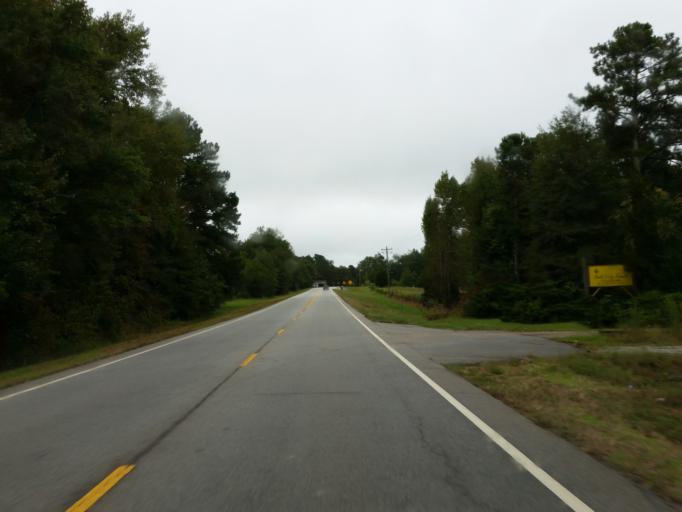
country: US
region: Georgia
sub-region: Lamar County
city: Barnesville
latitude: 33.0086
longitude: -84.1239
